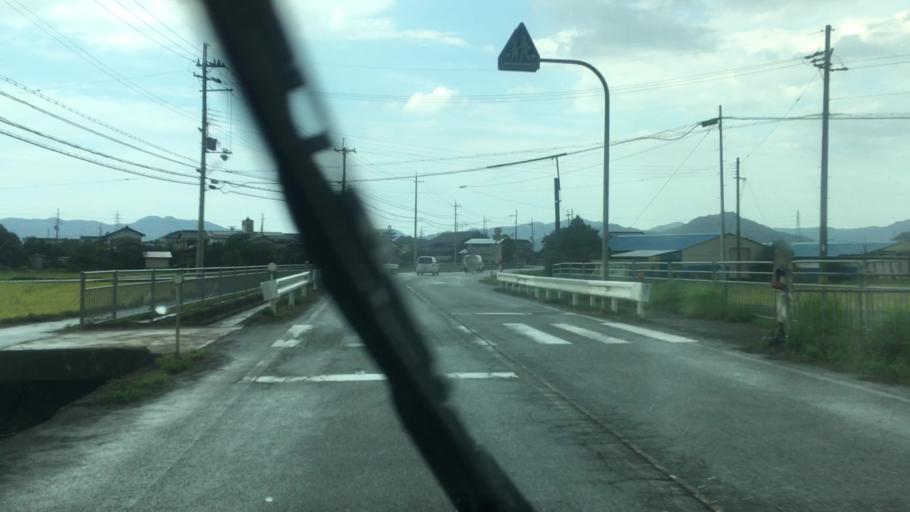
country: JP
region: Hyogo
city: Toyooka
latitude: 35.4988
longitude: 134.8179
